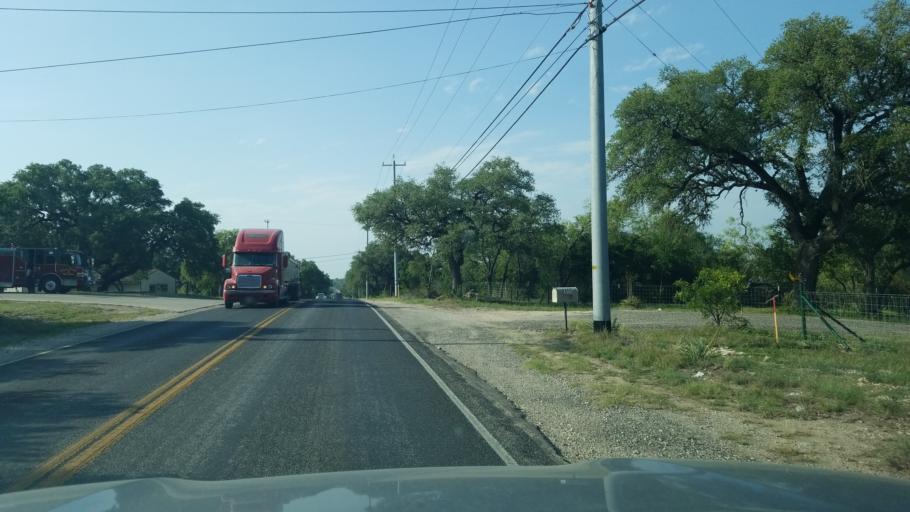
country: US
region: Texas
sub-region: Bexar County
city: Helotes
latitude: 29.4550
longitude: -98.7558
